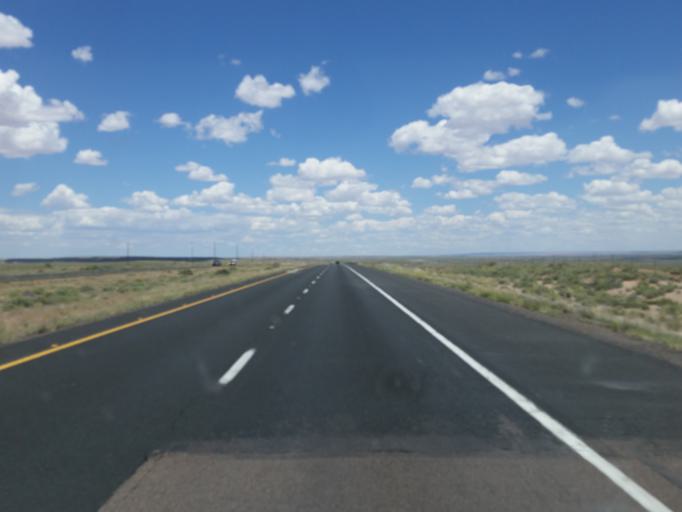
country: US
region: Arizona
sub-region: Navajo County
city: Holbrook
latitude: 34.9884
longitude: -110.0102
